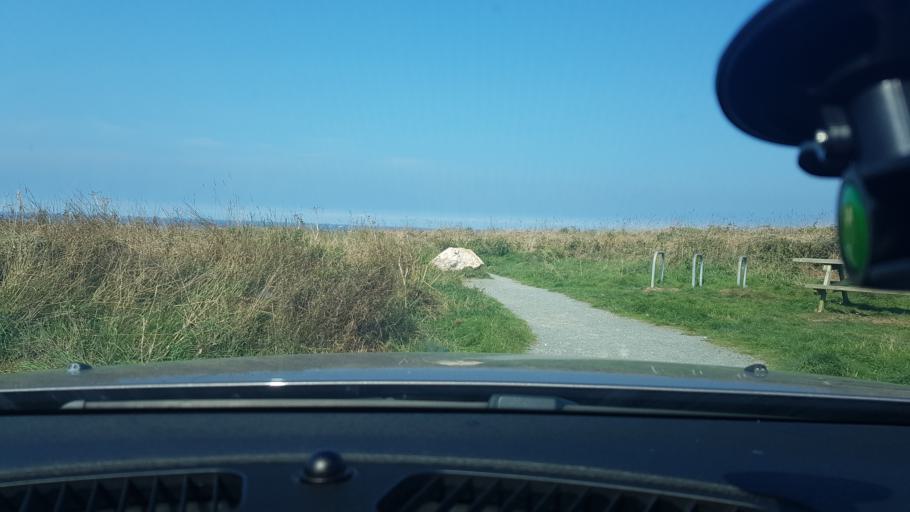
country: GB
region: England
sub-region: Cornwall
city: Tintagel
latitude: 50.6627
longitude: -4.7604
